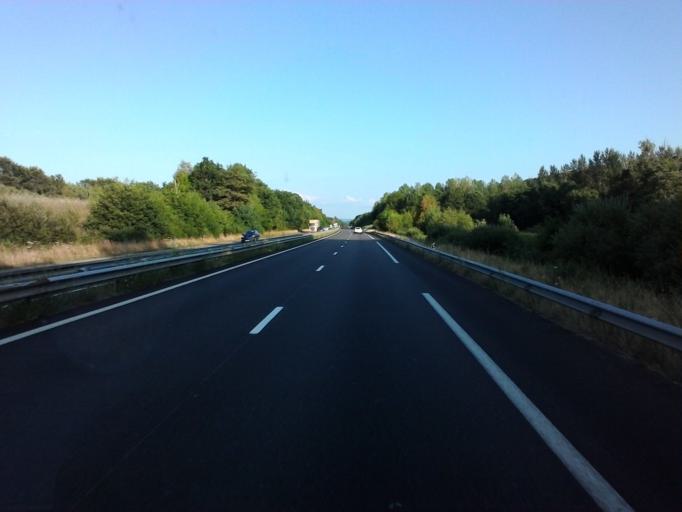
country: FR
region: Lorraine
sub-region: Departement des Vosges
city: Thaon-les-Vosges
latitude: 48.2458
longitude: 6.4049
